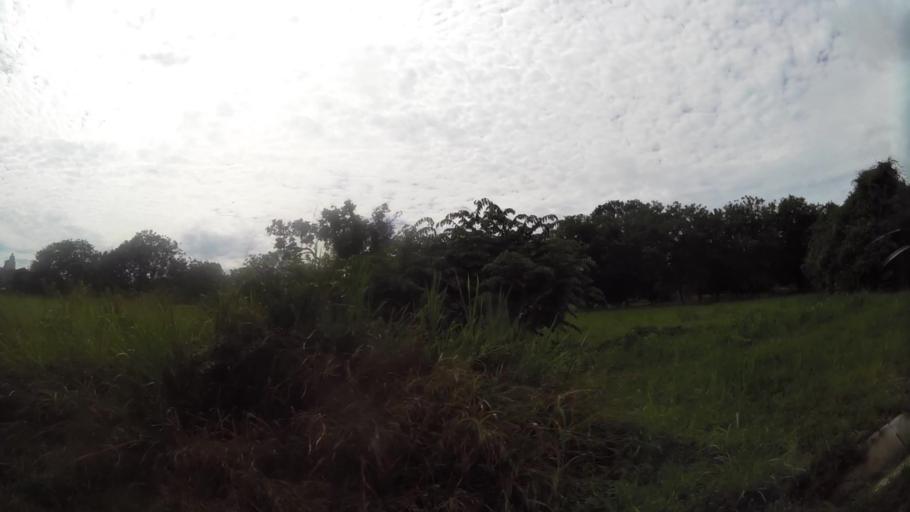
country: PA
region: Panama
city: Nueva Gorgona
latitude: 8.5452
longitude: -79.8922
